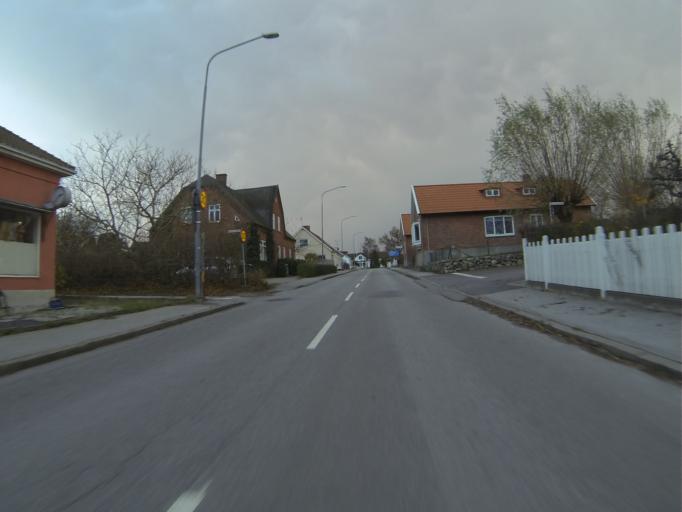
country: SE
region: Skane
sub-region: Lunds Kommun
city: Genarp
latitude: 55.6011
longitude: 13.4012
